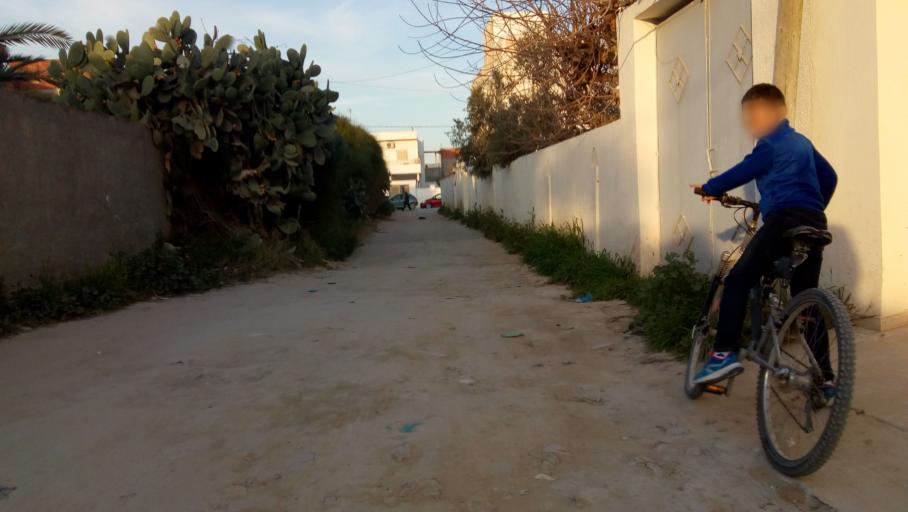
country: TN
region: Safaqis
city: Sfax
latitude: 34.7525
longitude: 10.7381
